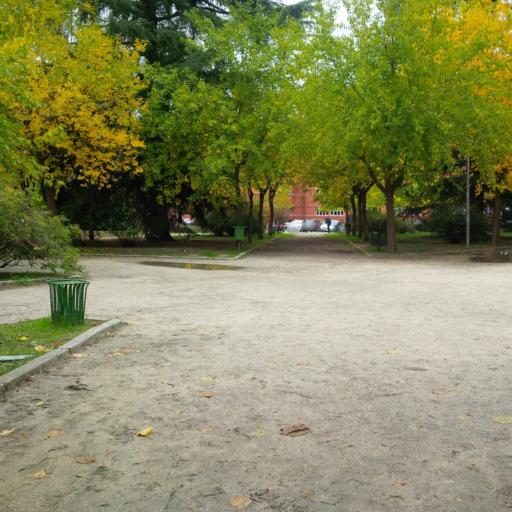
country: ES
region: Madrid
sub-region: Provincia de Madrid
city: Moncloa-Aravaca
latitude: 40.4500
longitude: -3.7260
